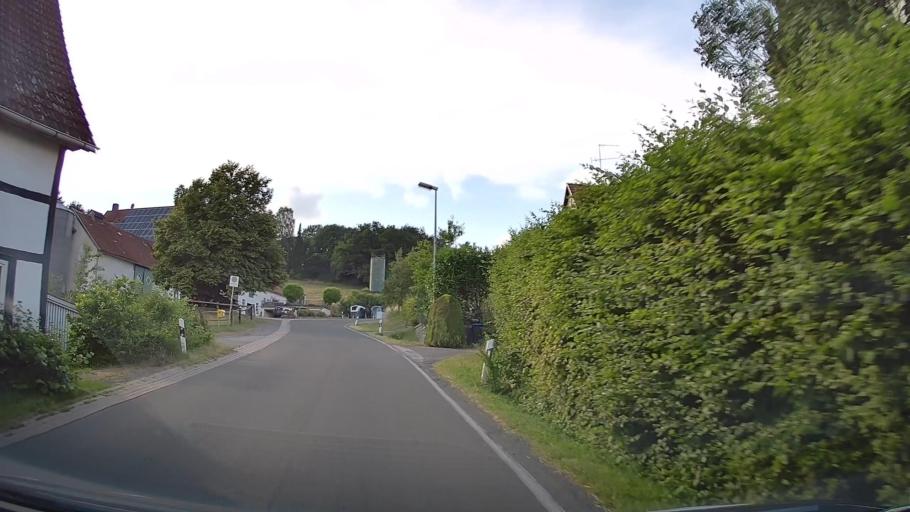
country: DE
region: North Rhine-Westphalia
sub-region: Regierungsbezirk Detmold
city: Barntrup
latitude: 51.9675
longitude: 9.1712
